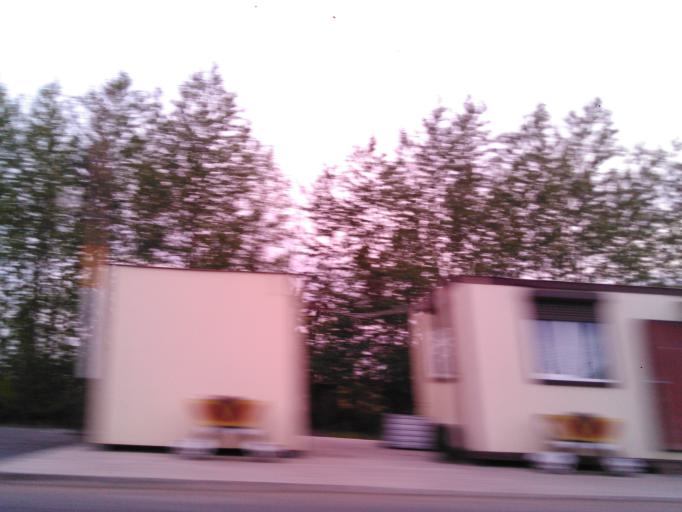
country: RU
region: Tatarstan
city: Russkiy Aktash
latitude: 55.0491
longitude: 52.0983
